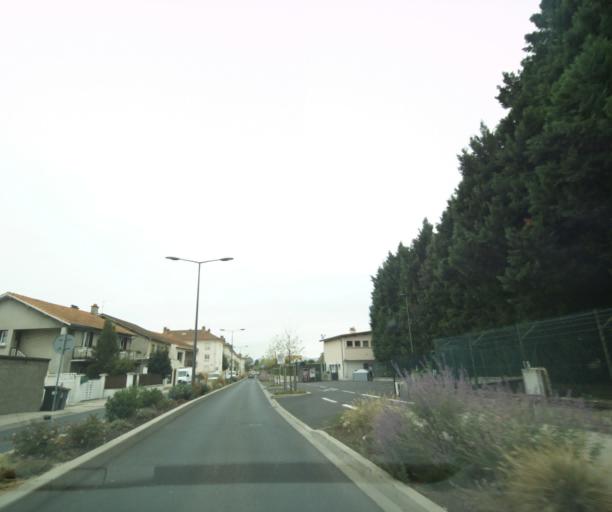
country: FR
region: Auvergne
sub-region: Departement du Puy-de-Dome
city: Gerzat
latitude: 45.8208
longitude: 3.1414
